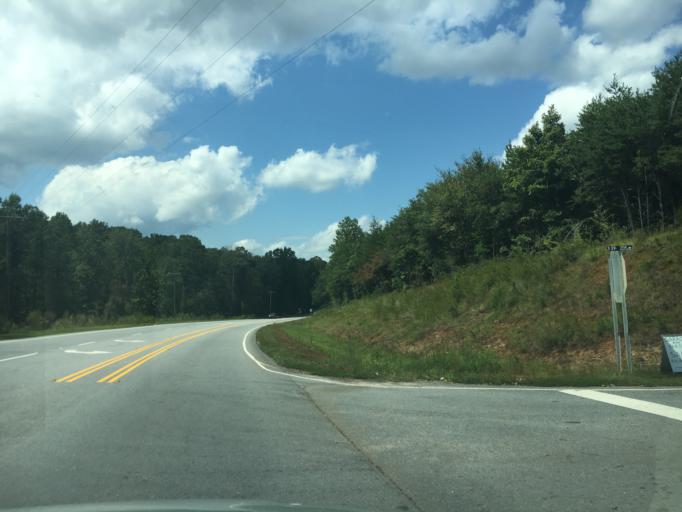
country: US
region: South Carolina
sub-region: Greenville County
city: Berea
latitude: 34.8865
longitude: -82.5013
